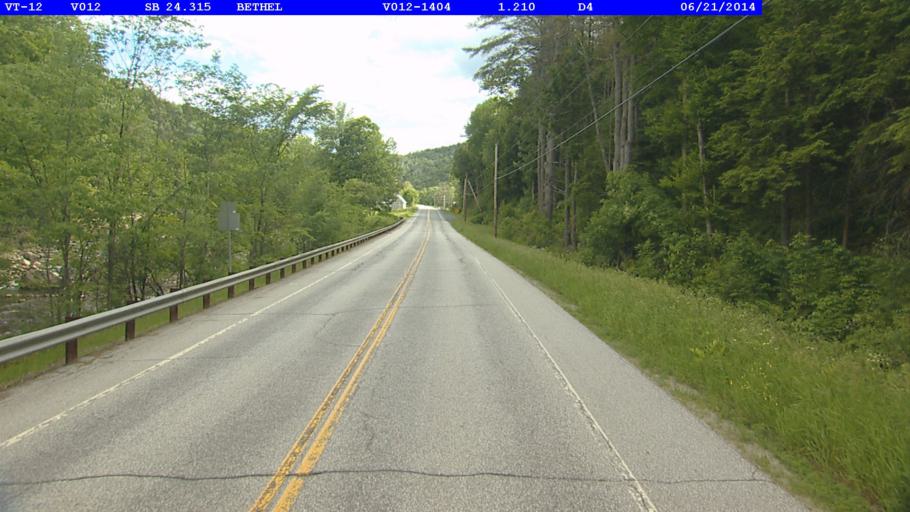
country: US
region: Vermont
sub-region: Orange County
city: Randolph
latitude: 43.8076
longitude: -72.6520
